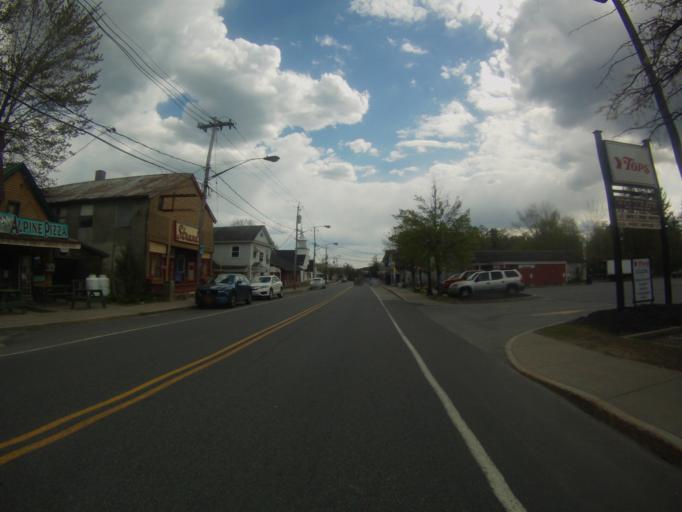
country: US
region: New York
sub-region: Essex County
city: Ticonderoga
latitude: 43.8377
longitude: -73.7614
